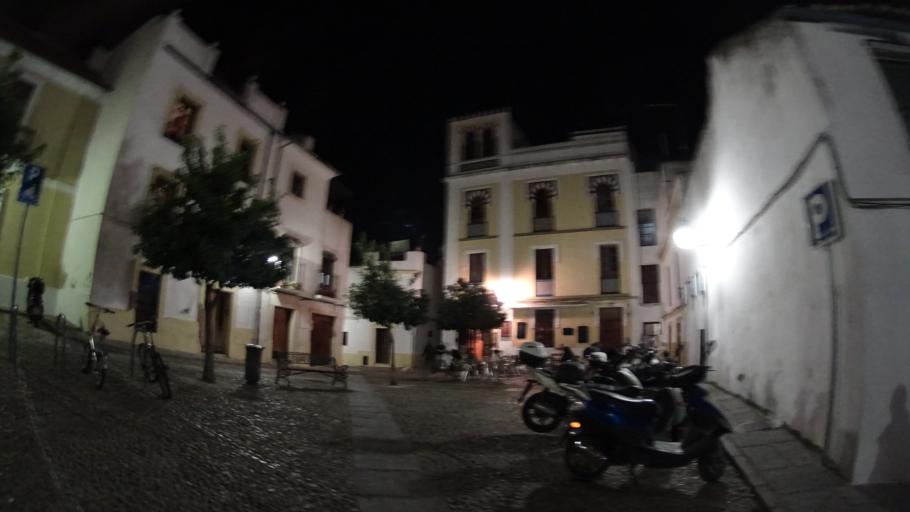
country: ES
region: Andalusia
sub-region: Province of Cordoba
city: Cordoba
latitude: 37.8796
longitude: -4.7777
